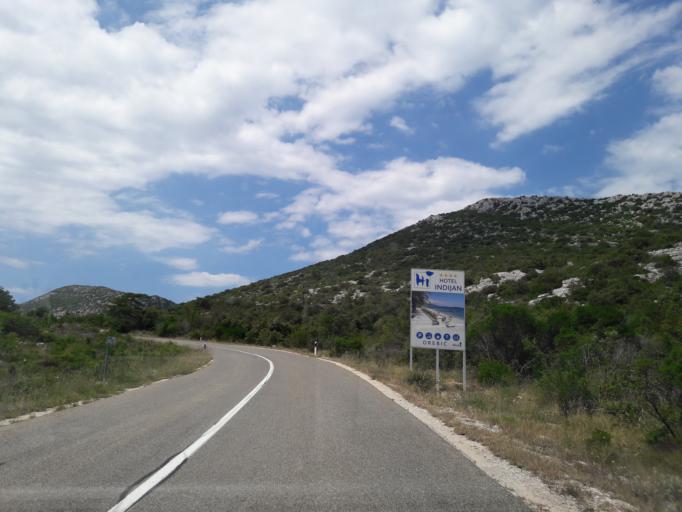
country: HR
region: Dubrovacko-Neretvanska
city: Orebic
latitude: 42.9722
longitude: 17.2770
